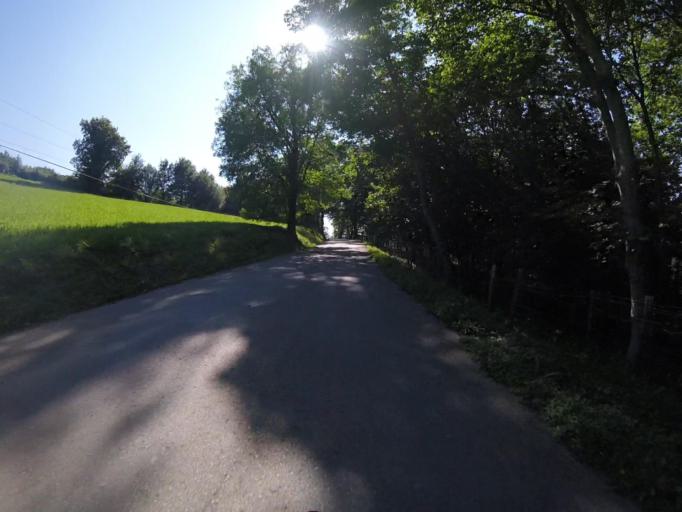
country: ES
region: Basque Country
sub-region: Provincia de Guipuzcoa
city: Astigarraga
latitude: 43.2652
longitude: -1.9318
